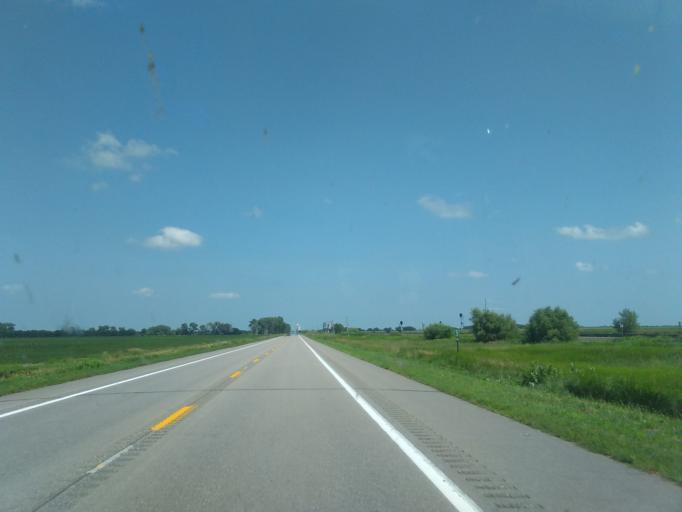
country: US
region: Nebraska
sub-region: Phelps County
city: Holdrege
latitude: 40.7237
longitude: -99.4227
